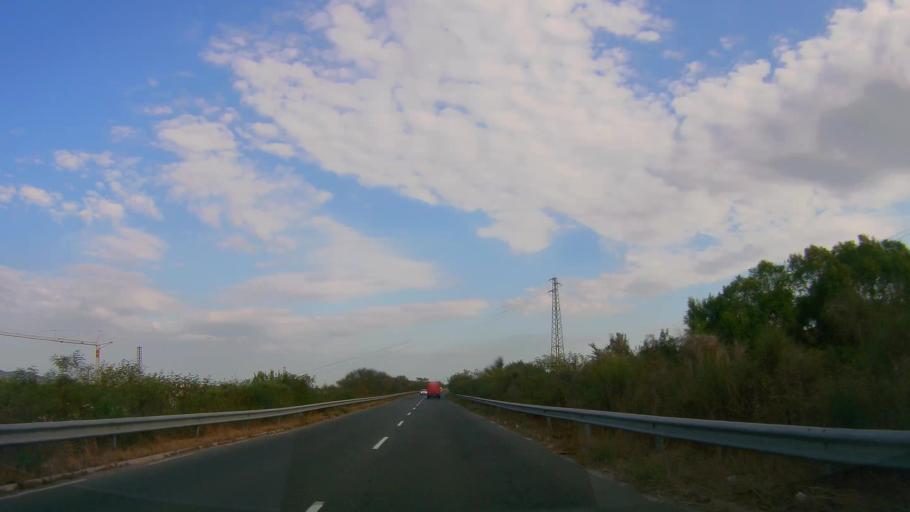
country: BG
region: Burgas
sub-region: Obshtina Sozopol
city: Sozopol
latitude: 42.3937
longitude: 27.6760
